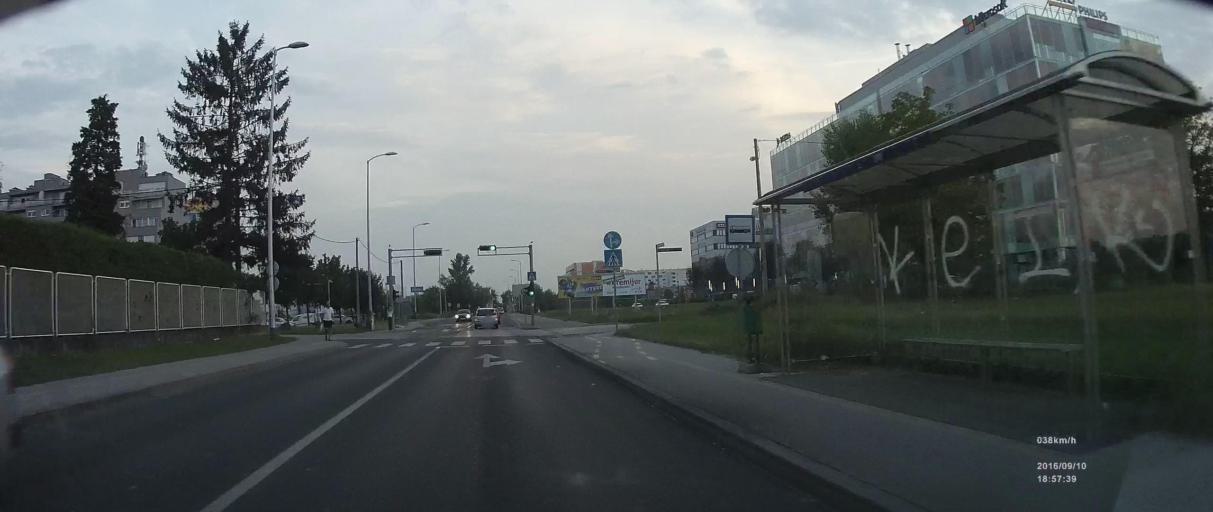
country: HR
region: Grad Zagreb
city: Novi Zagreb
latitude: 45.7652
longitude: 15.9809
